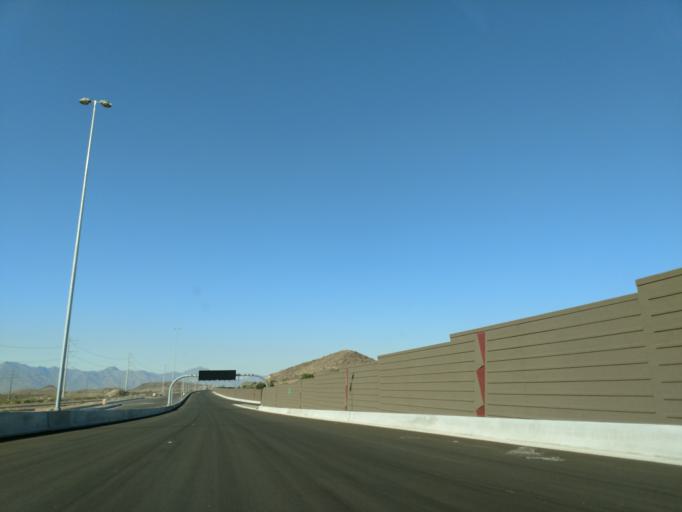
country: US
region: Arizona
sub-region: Maricopa County
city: Guadalupe
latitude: 33.2921
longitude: -112.0336
